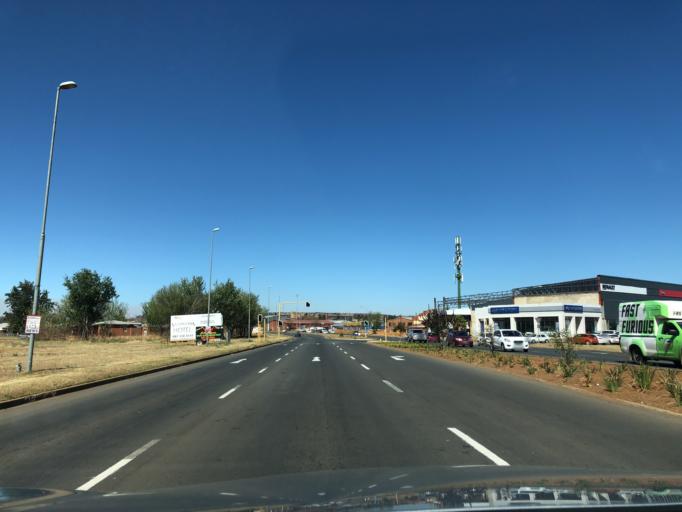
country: ZA
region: KwaZulu-Natal
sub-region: Amajuba District Municipality
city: Newcastle
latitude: -27.7483
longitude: 29.9376
